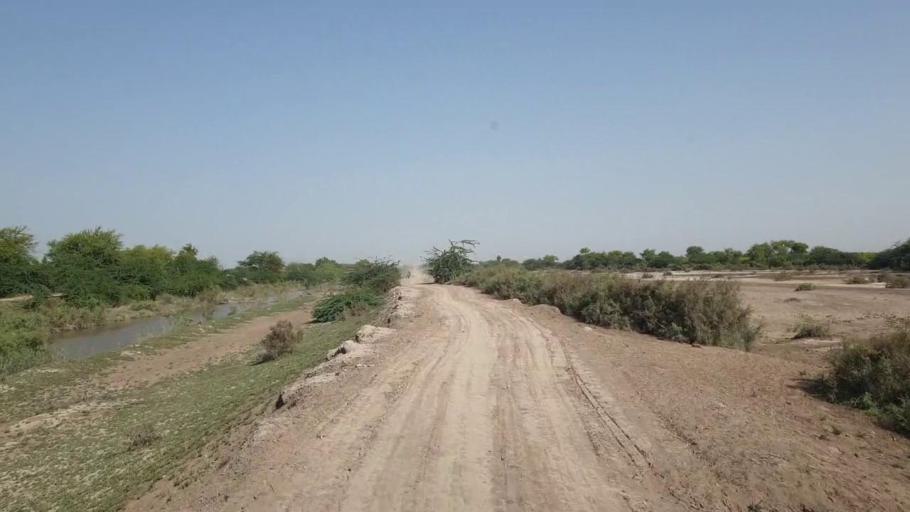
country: PK
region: Sindh
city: Tando Bago
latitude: 24.6648
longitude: 69.0673
